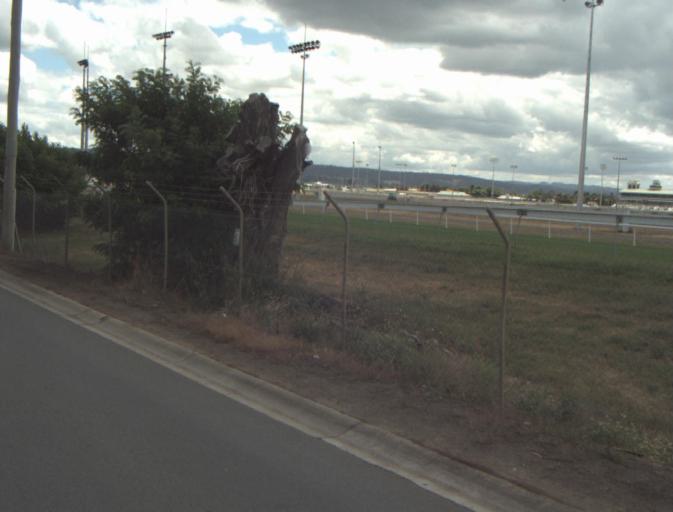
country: AU
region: Tasmania
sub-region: Launceston
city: Newnham
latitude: -41.4057
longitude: 147.1458
